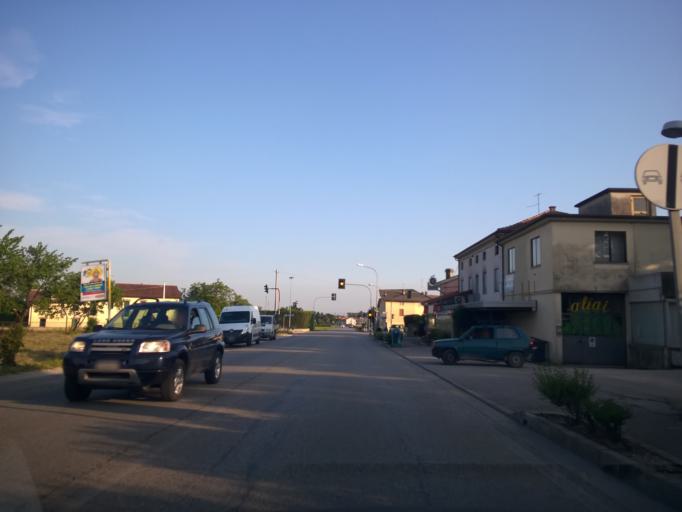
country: IT
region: Veneto
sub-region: Provincia di Vicenza
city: Centrale
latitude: 45.7252
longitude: 11.4665
